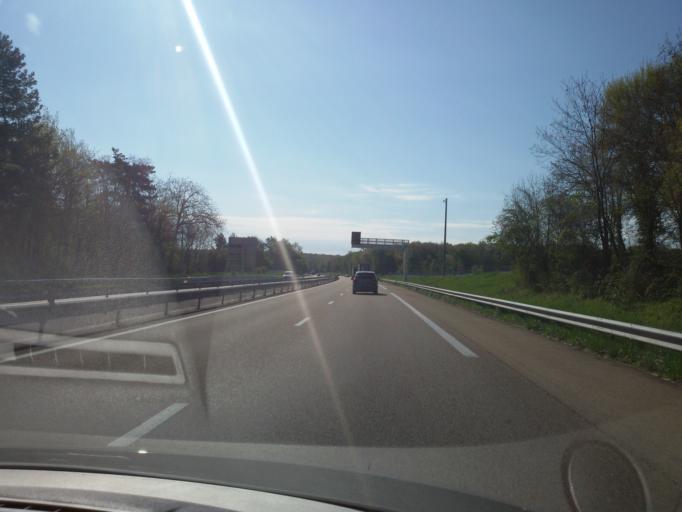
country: FR
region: Bourgogne
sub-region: Departement de l'Yonne
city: Vermenton
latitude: 47.7192
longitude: 3.7597
